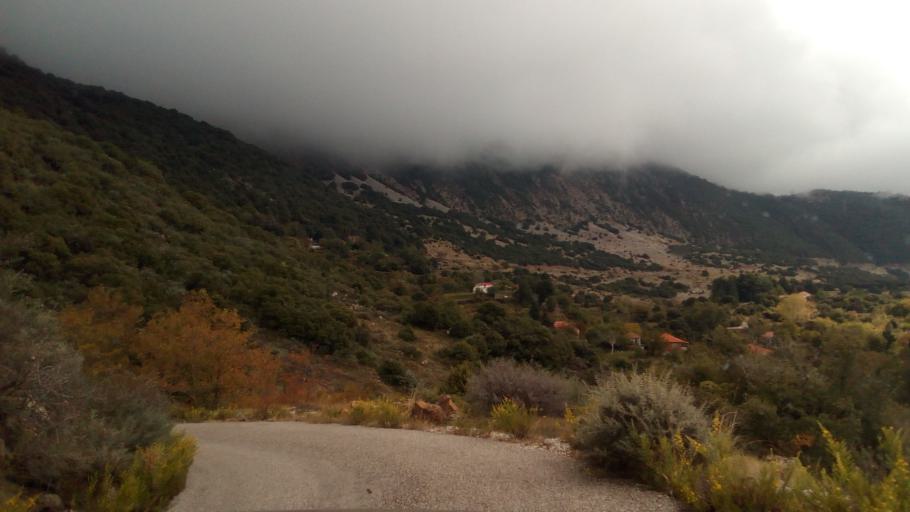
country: GR
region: West Greece
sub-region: Nomos Aitolias kai Akarnanias
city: Nafpaktos
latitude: 38.5001
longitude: 21.8385
